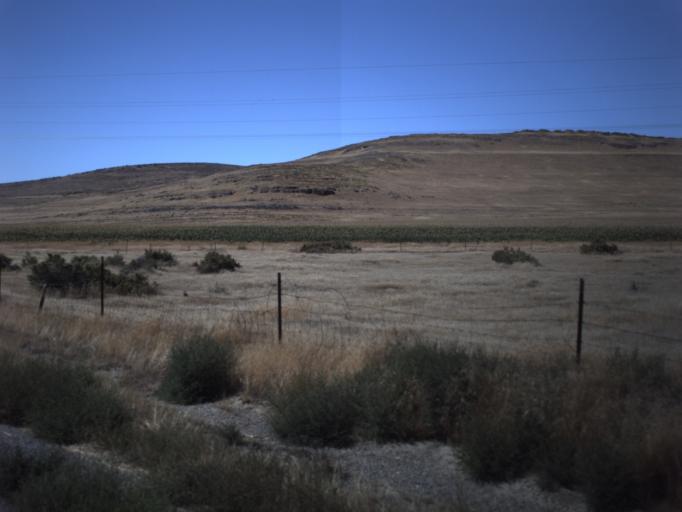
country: US
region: Utah
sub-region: Utah County
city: Genola
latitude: 40.1260
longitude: -111.9582
